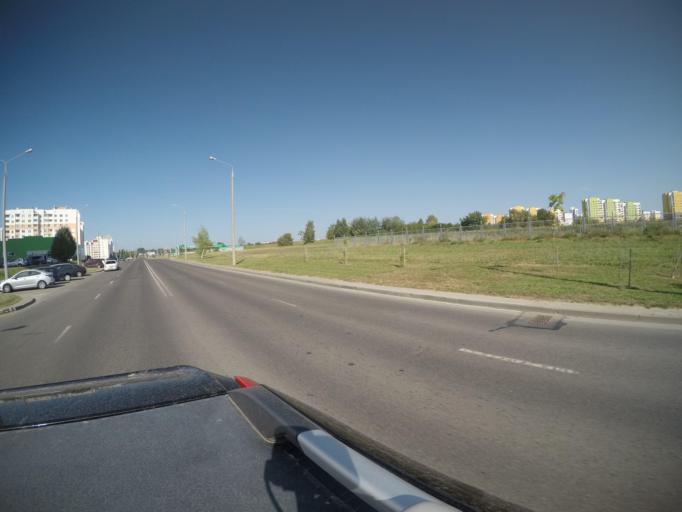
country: BY
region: Grodnenskaya
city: Hrodna
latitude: 53.7140
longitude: 23.8640
